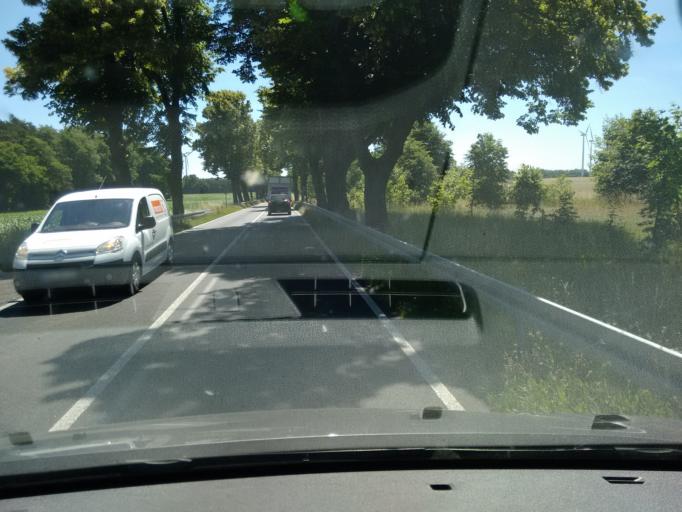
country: DE
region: Brandenburg
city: Beeskow
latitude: 52.2111
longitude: 14.2242
